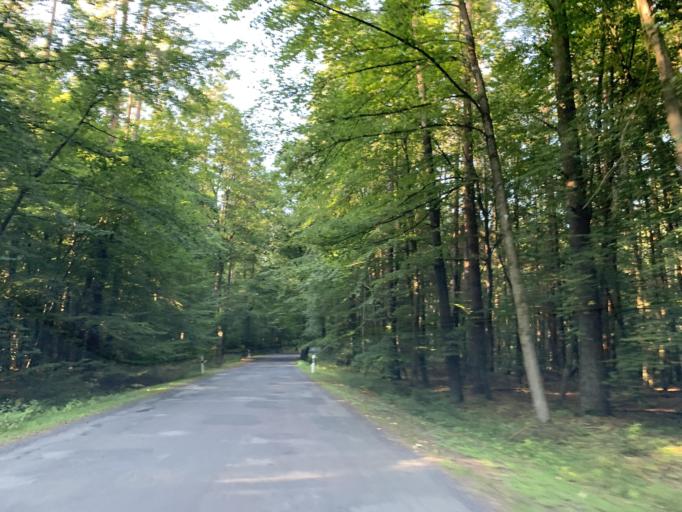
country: DE
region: Mecklenburg-Vorpommern
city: Carpin
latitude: 53.3414
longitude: 13.2416
